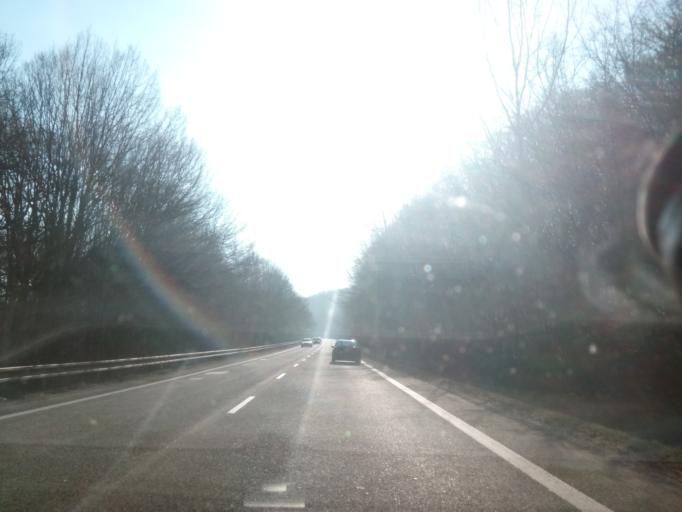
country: SK
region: Kosicky
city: Kosice
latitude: 48.7379
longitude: 21.3675
